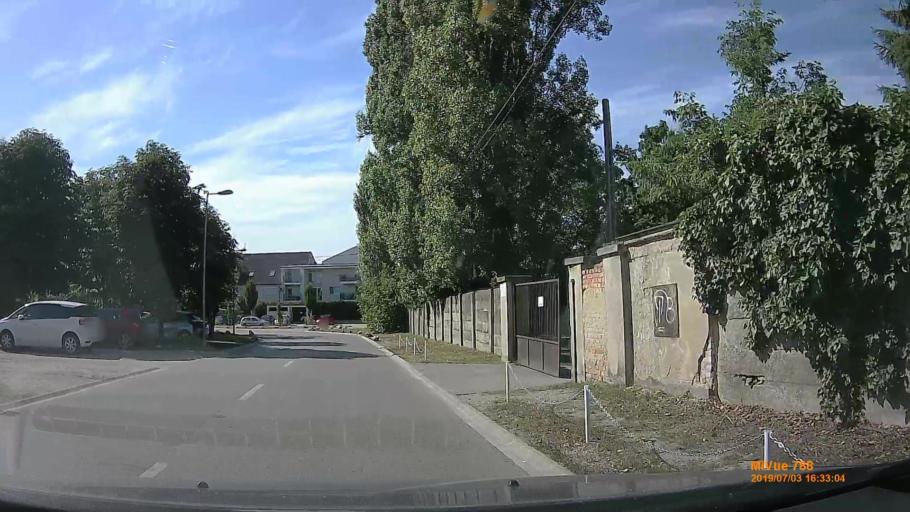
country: HU
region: Gyor-Moson-Sopron
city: Gyor
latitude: 47.7035
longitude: 17.6368
